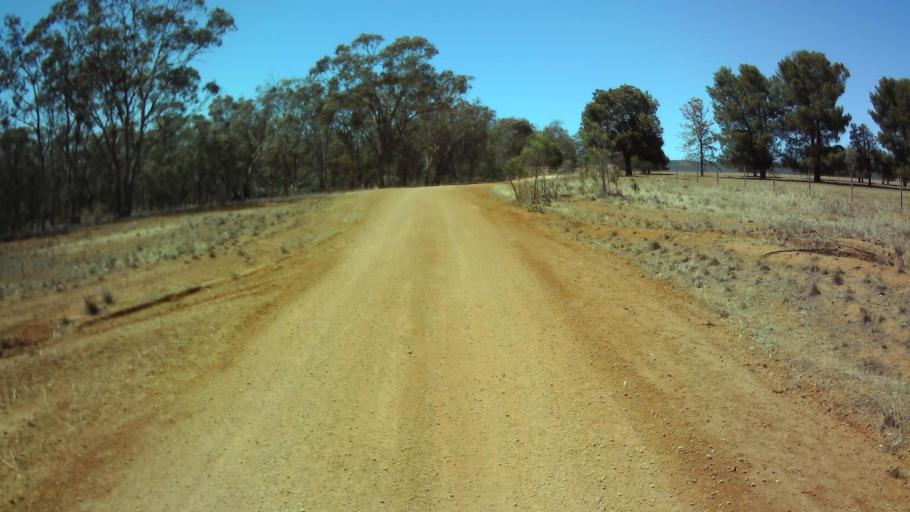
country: AU
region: New South Wales
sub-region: Weddin
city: Grenfell
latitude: -33.9443
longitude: 148.0797
